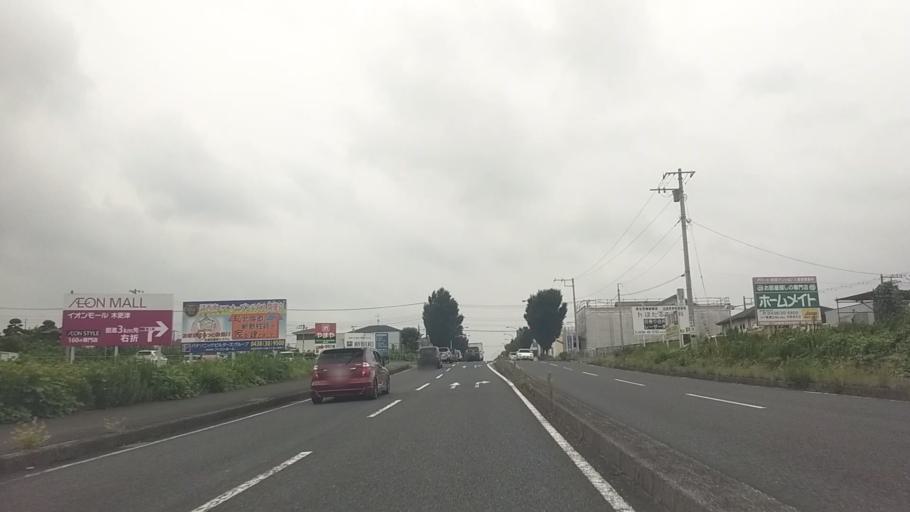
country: JP
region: Chiba
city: Kisarazu
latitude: 35.3828
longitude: 139.9673
